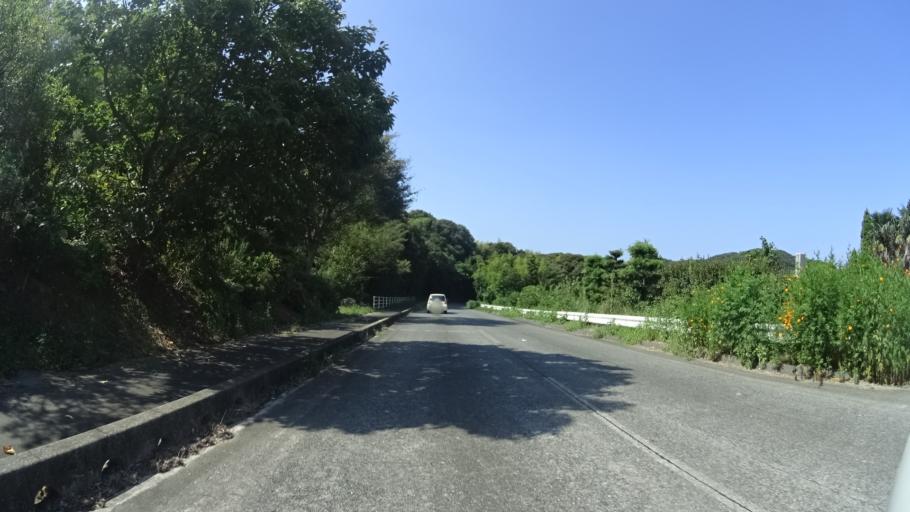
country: JP
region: Yamaguchi
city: Shimonoseki
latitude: 34.0936
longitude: 130.8860
